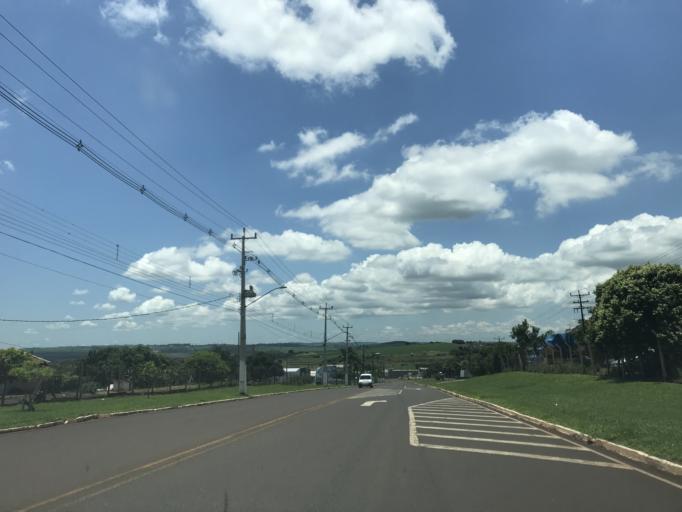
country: BR
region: Parana
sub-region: Marialva
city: Marialva
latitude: -23.4947
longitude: -51.7808
